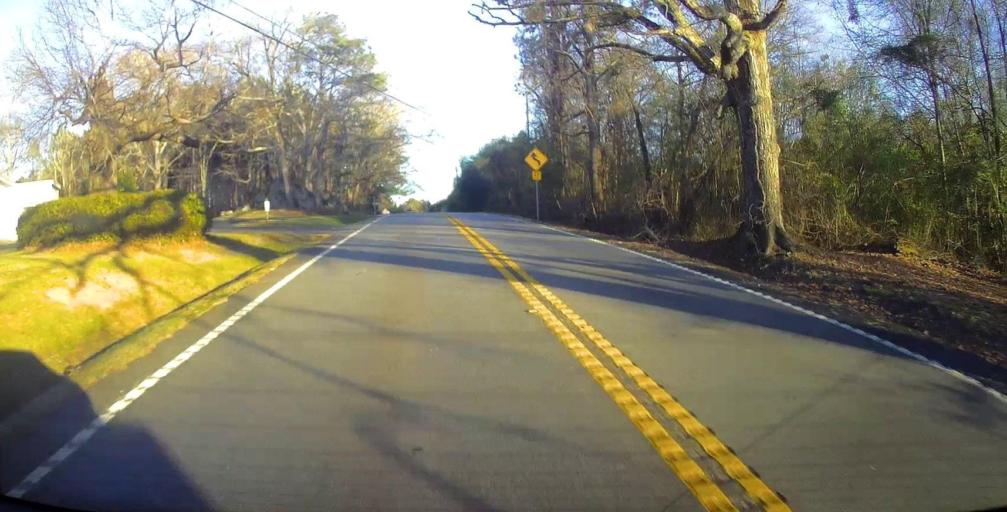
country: US
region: Georgia
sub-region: Harris County
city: Hamilton
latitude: 32.6549
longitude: -84.8682
